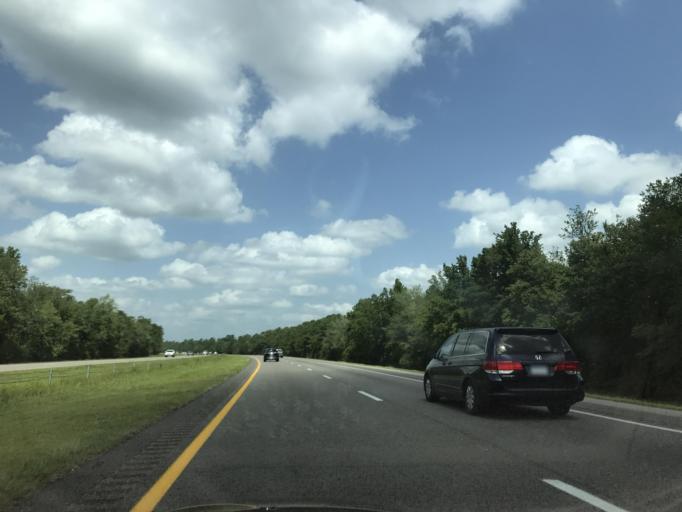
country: US
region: North Carolina
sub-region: Pender County
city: Burgaw
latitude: 34.5062
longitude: -77.8771
